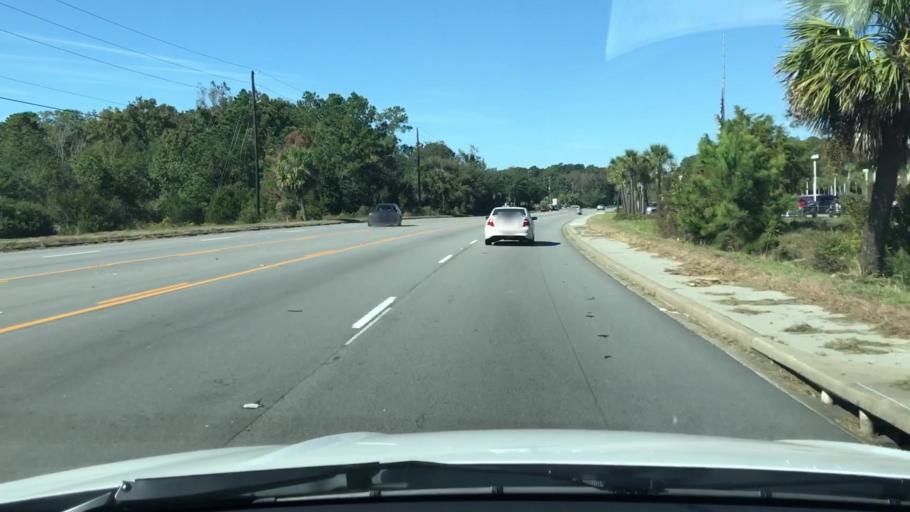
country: US
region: South Carolina
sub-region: Beaufort County
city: Burton
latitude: 32.4458
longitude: -80.7290
